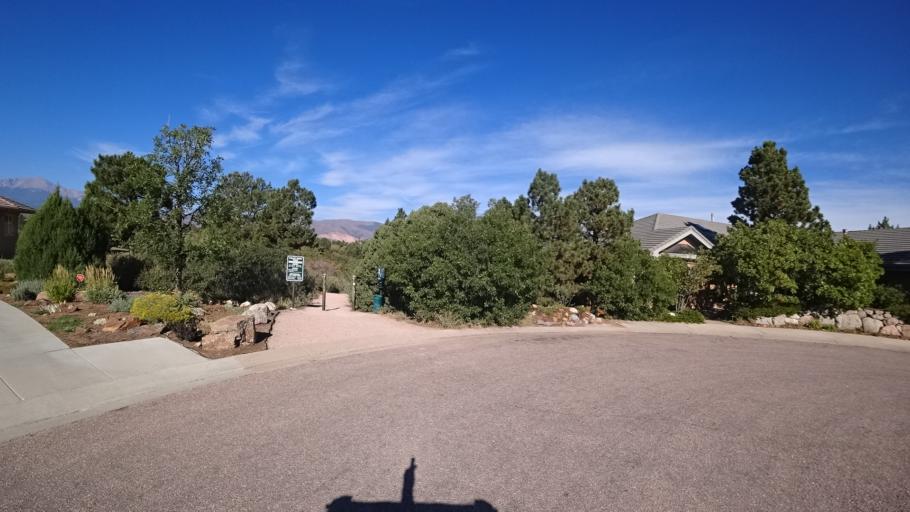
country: US
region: Colorado
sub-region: El Paso County
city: Colorado Springs
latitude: 38.9115
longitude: -104.8025
